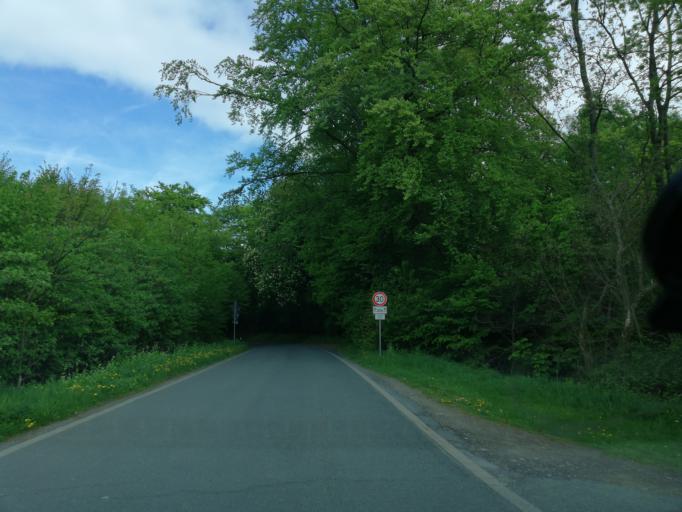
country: DE
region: North Rhine-Westphalia
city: Gevelsberg
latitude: 51.3537
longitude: 7.3004
